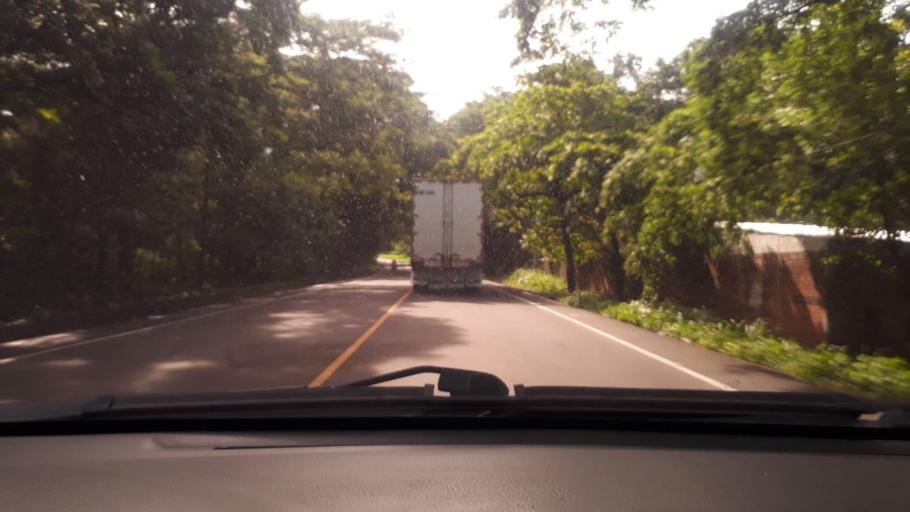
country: SV
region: Ahuachapan
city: San Francisco Menendez
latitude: 13.8788
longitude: -90.1252
